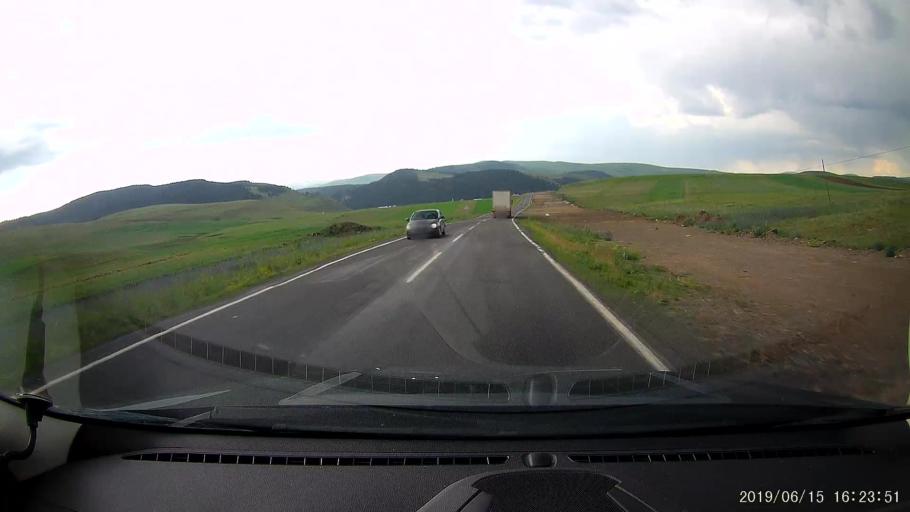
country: TR
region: Ardahan
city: Hanak
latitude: 41.1730
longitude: 42.8667
